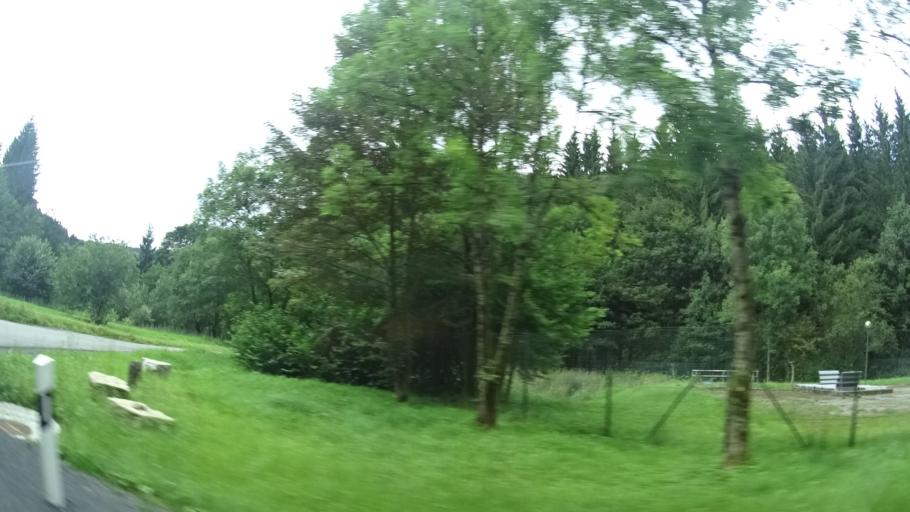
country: DE
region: Thuringia
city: Judenbach
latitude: 50.3998
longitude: 11.2600
